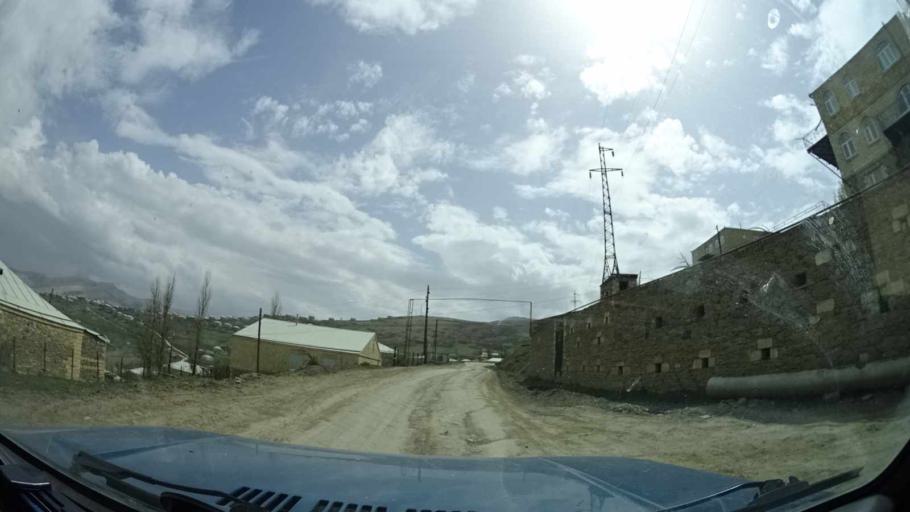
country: RU
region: Dagestan
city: Kubachi
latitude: 42.0961
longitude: 47.5942
